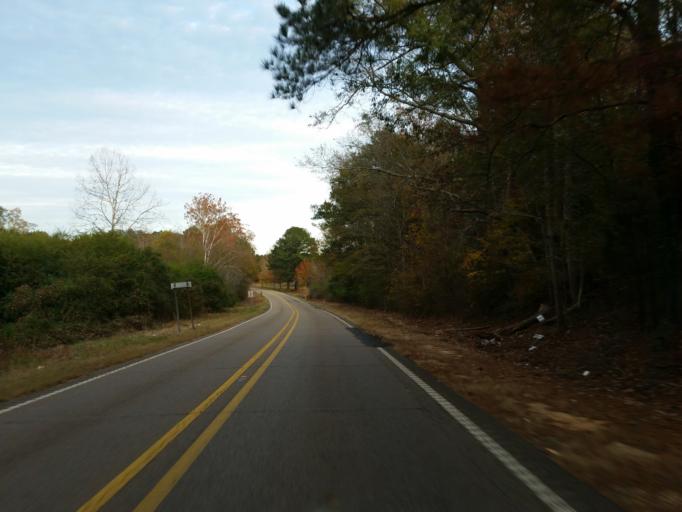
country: US
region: Mississippi
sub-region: Lauderdale County
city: Marion
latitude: 32.4182
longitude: -88.5014
